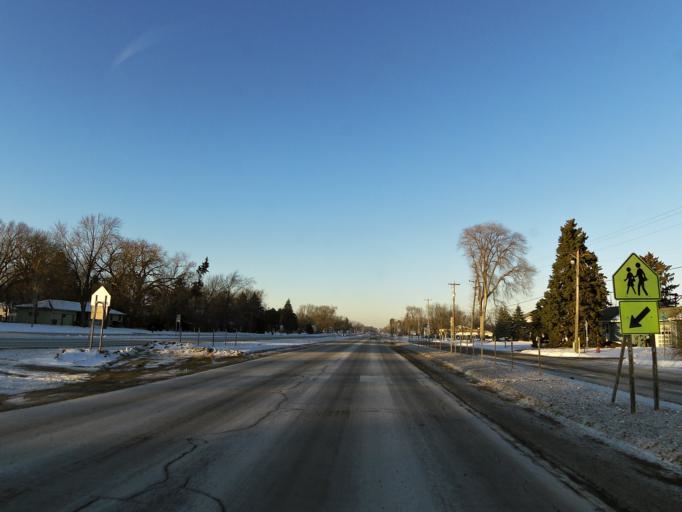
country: US
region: Minnesota
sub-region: Dakota County
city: Farmington
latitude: 44.6333
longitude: -93.1369
